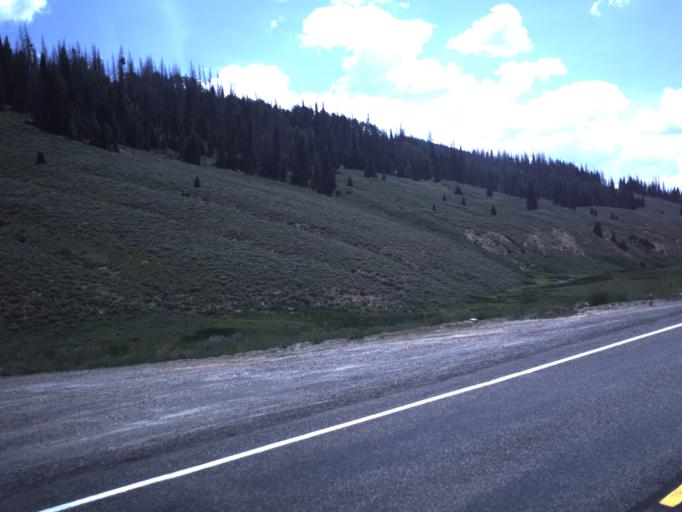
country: US
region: Utah
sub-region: Sanpete County
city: Fairview
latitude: 39.6763
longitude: -111.2438
